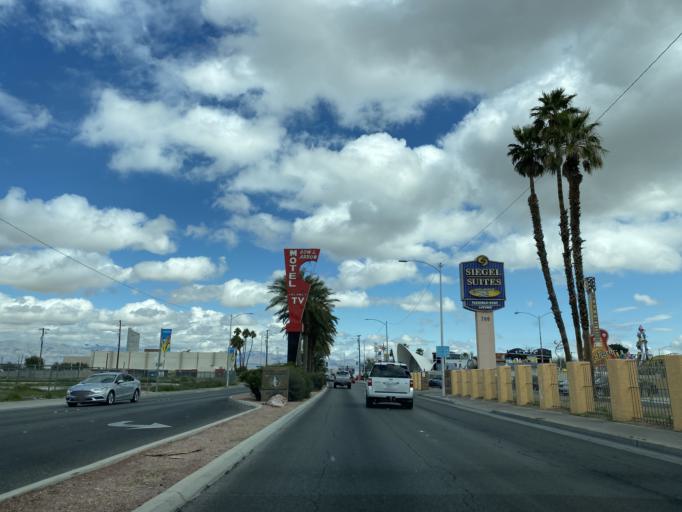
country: US
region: Nevada
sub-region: Clark County
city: Las Vegas
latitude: 36.1760
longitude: -115.1363
